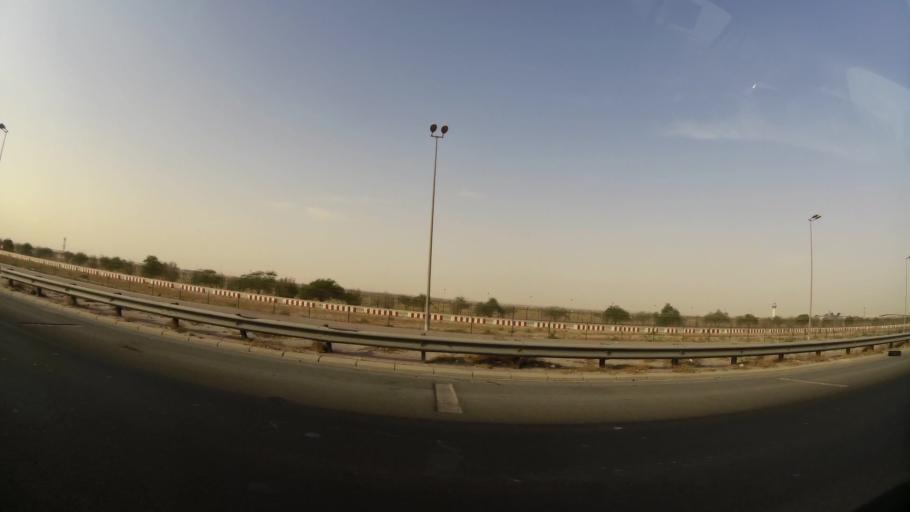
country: KW
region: Al Farwaniyah
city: Janub as Surrah
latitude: 29.2189
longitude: 47.9996
